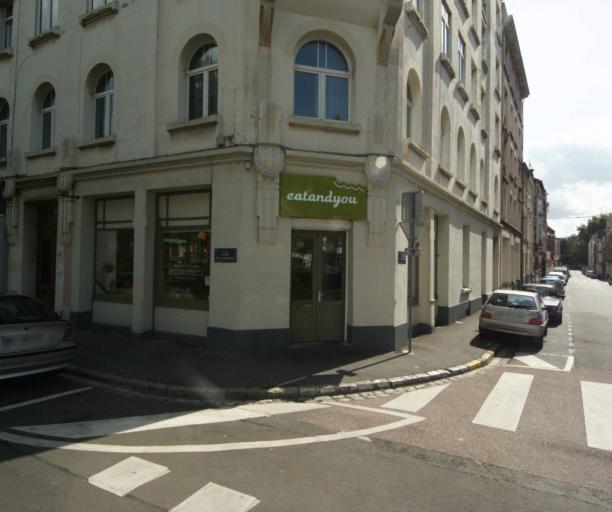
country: FR
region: Nord-Pas-de-Calais
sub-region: Departement du Nord
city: La Madeleine
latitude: 50.6463
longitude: 3.0761
